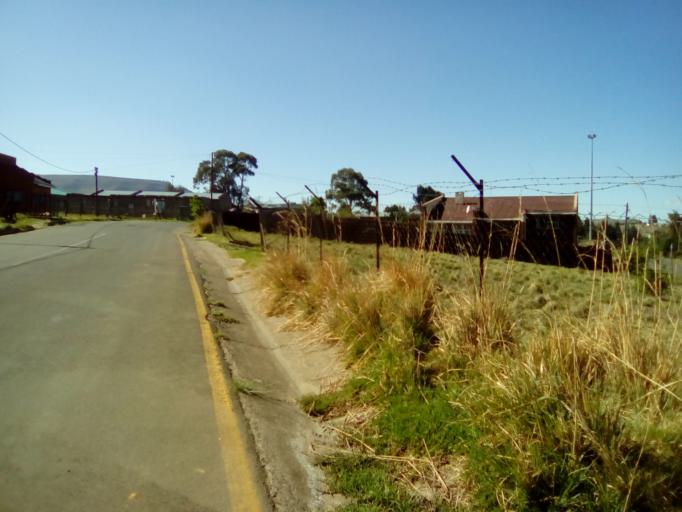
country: LS
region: Qacha's Nek
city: Qacha's Nek
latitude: -30.1069
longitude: 28.6817
